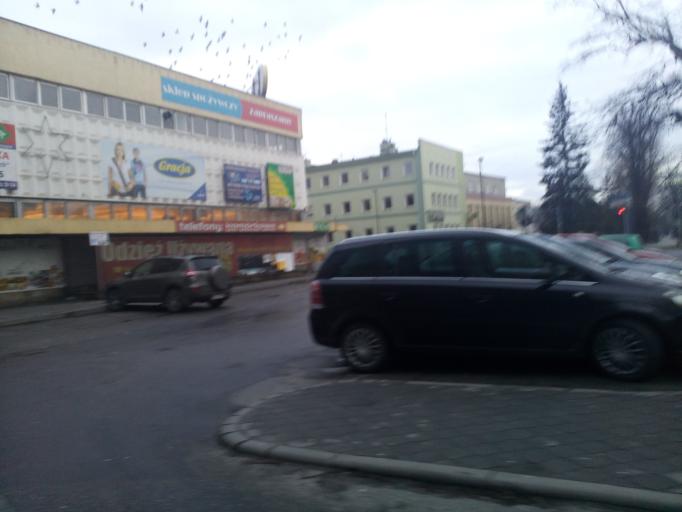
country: PL
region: Lesser Poland Voivodeship
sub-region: Powiat nowosadecki
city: Nowy Sacz
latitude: 49.6126
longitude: 20.6982
